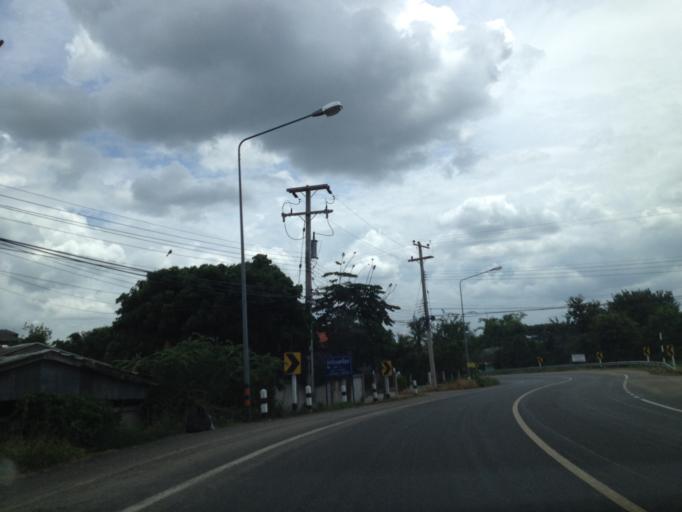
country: TH
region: Chiang Mai
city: San Pa Tong
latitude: 18.6353
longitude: 98.8496
